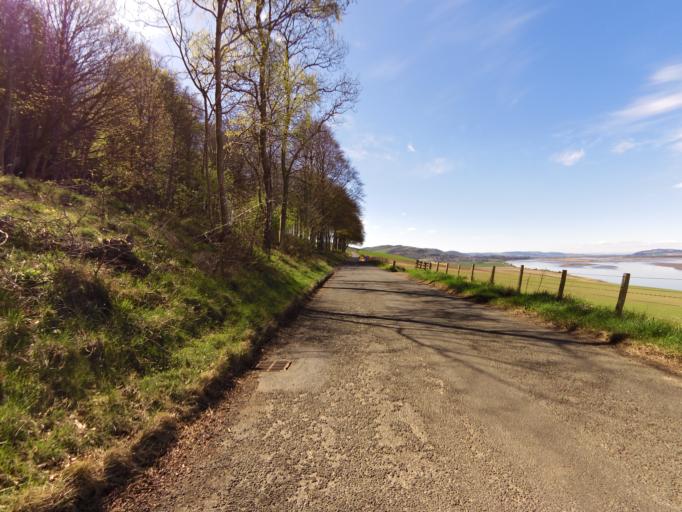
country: GB
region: Scotland
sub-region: Perth and Kinross
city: Errol
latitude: 56.3649
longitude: -3.1874
